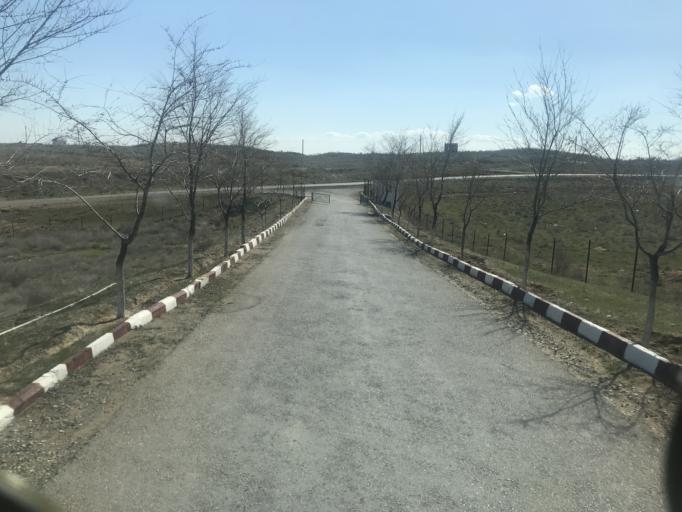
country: KZ
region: Ongtustik Qazaqstan
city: Shardara
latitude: 41.2476
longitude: 67.9027
